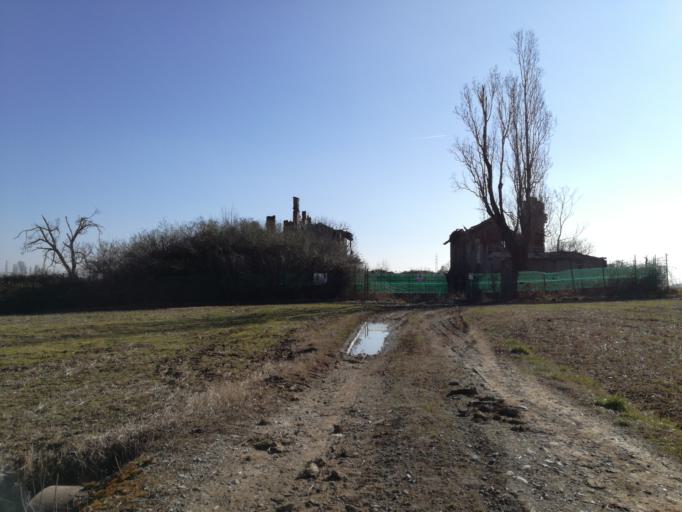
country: IT
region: Lombardy
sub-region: Provincia di Lecco
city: Verderio Inferiore
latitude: 45.6530
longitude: 9.4351
